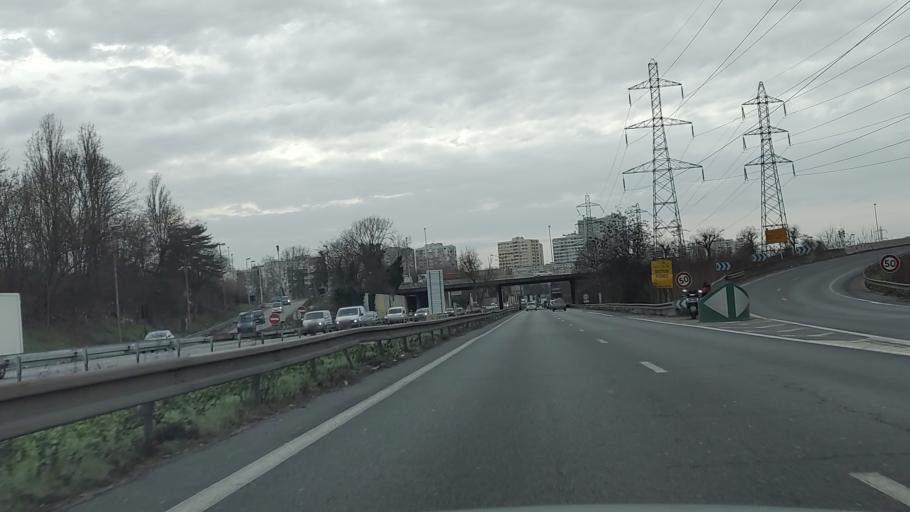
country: FR
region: Ile-de-France
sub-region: Departement des Hauts-de-Seine
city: Gennevilliers
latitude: 48.9343
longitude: 2.2840
